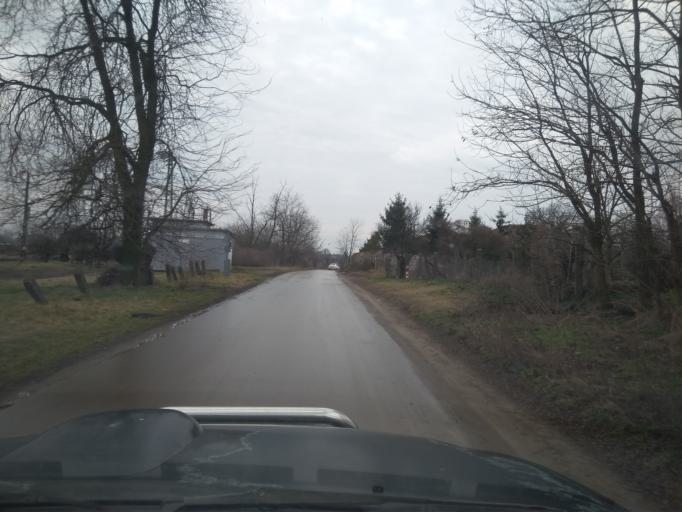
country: HU
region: Szabolcs-Szatmar-Bereg
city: Nyiregyhaza
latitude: 47.9664
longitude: 21.6852
